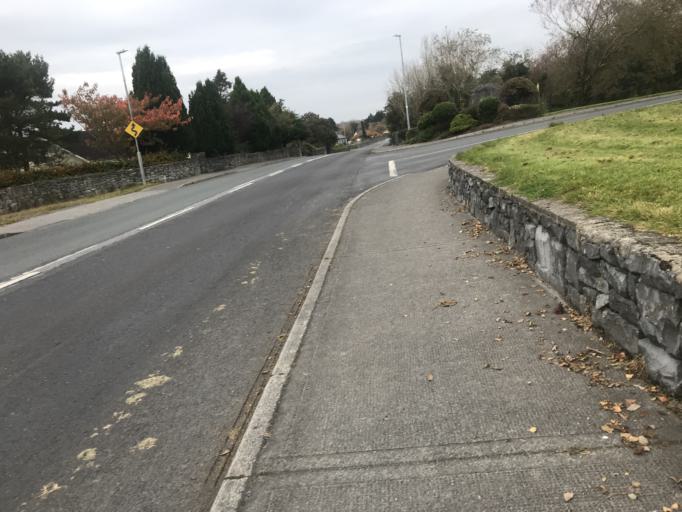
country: IE
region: Connaught
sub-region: County Galway
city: Gaillimh
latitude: 53.2943
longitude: -9.0530
